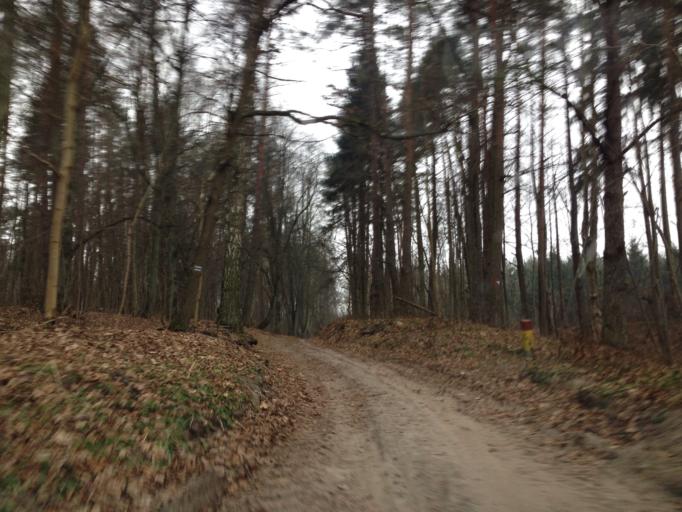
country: PL
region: Warmian-Masurian Voivodeship
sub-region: Powiat ketrzynski
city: Reszel
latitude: 54.0254
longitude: 21.2135
